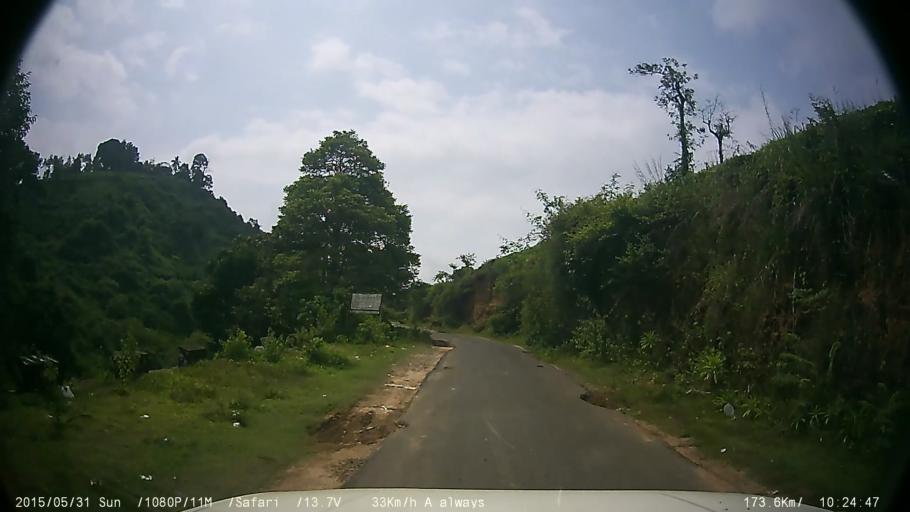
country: IN
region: Kerala
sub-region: Wayanad
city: Kalpetta
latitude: 11.5323
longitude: 76.1374
